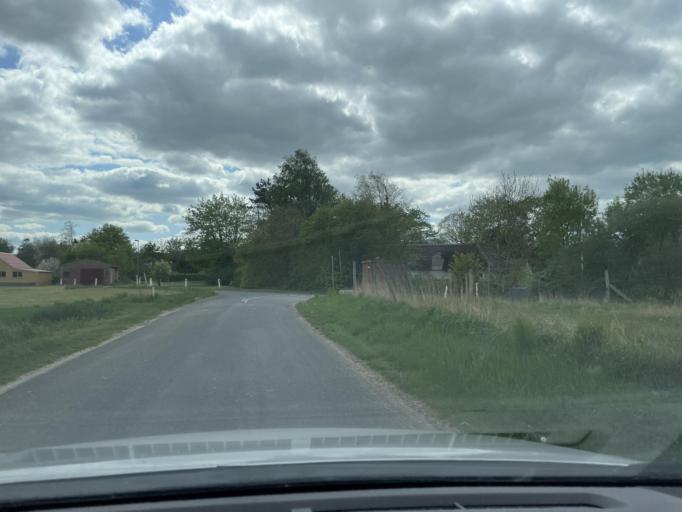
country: DK
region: Central Jutland
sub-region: Skanderborg Kommune
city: Skanderborg
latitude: 55.9210
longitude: 9.9692
